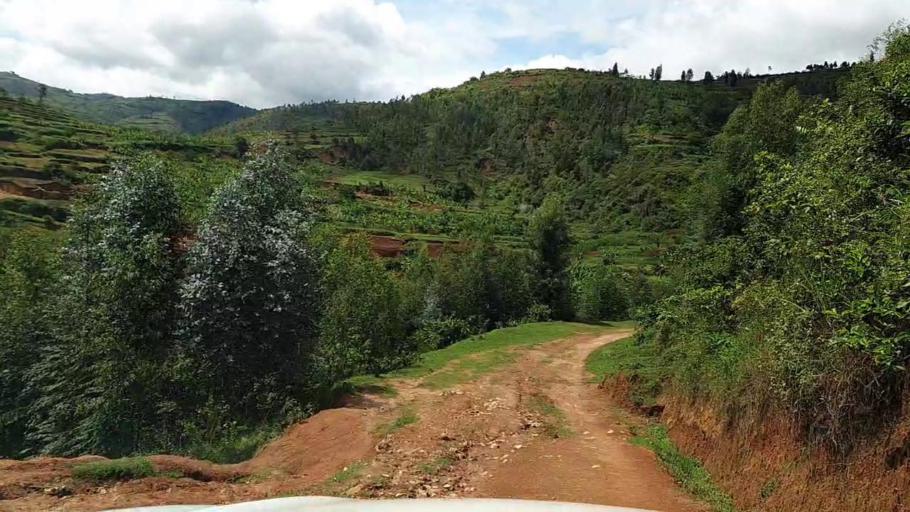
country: RW
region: Southern Province
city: Gikongoro
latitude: -2.3615
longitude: 29.5406
